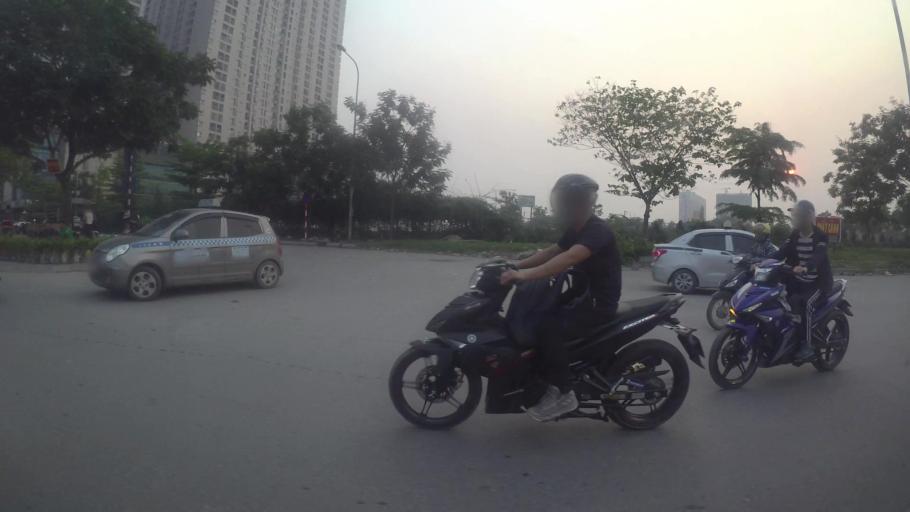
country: VN
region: Ha Noi
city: Cau Dien
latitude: 21.0098
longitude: 105.7306
